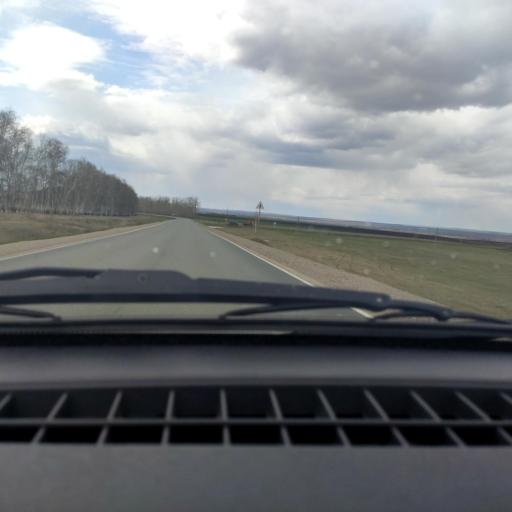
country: RU
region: Bashkortostan
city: Kushnarenkovo
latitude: 55.0582
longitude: 55.1674
